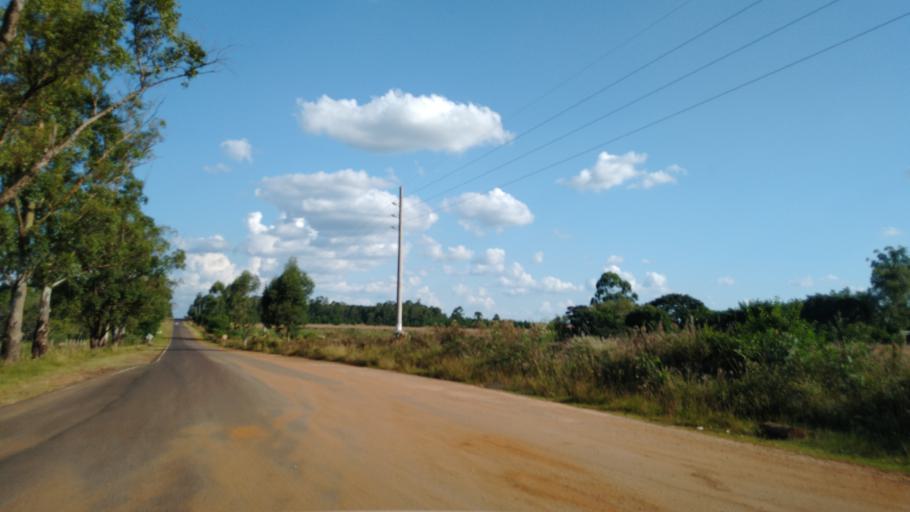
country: PY
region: Itapua
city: San Juan del Parana
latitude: -27.3711
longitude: -55.9925
